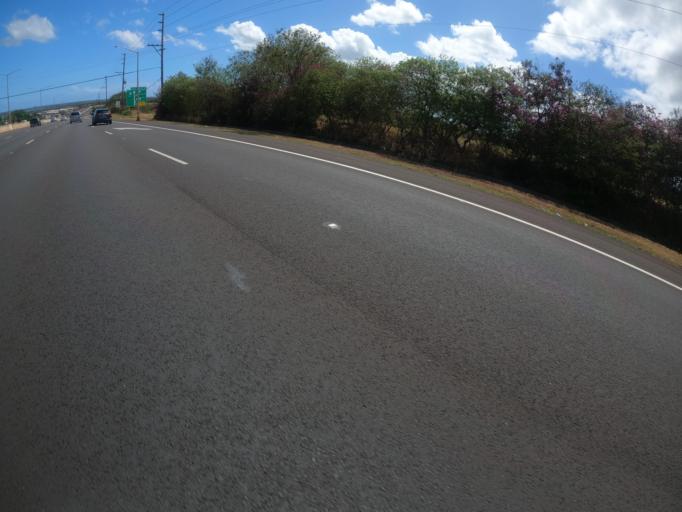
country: US
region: Hawaii
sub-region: Honolulu County
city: Royal Kunia
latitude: 21.3821
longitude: -158.0309
